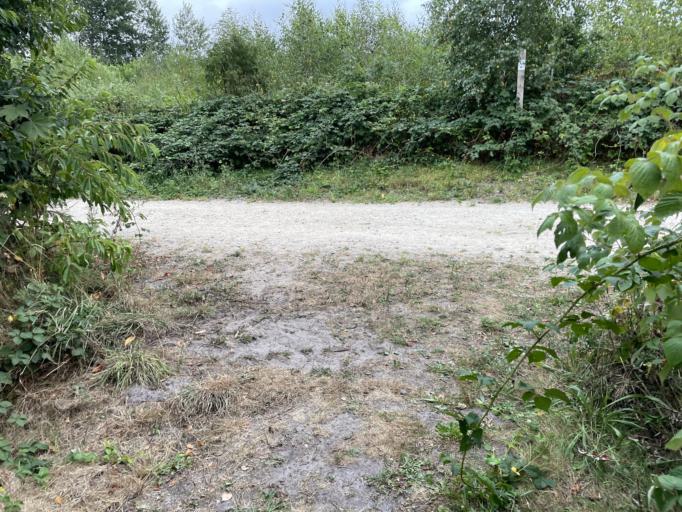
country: DE
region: Schleswig-Holstein
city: Mildstedt
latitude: 54.4705
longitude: 9.1135
